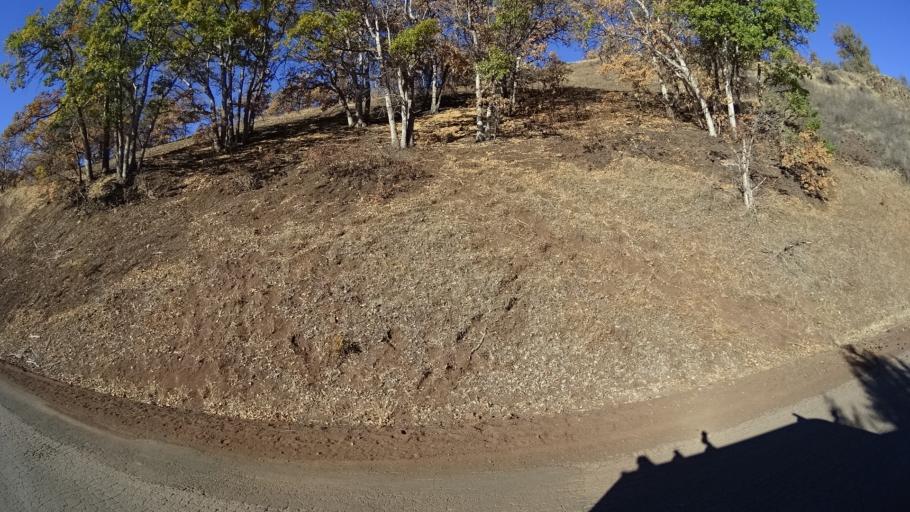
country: US
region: California
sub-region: Siskiyou County
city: Montague
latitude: 41.9711
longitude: -122.4394
